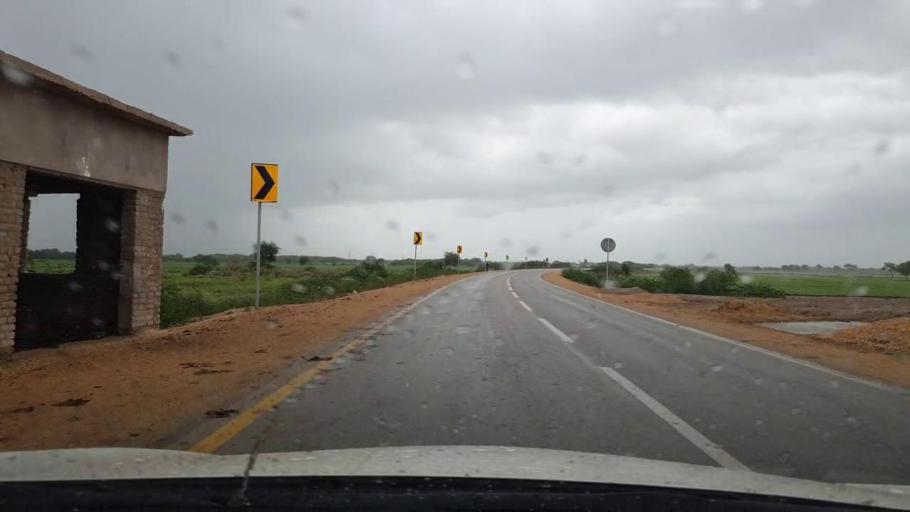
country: PK
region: Sindh
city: Badin
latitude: 24.6558
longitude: 68.6799
